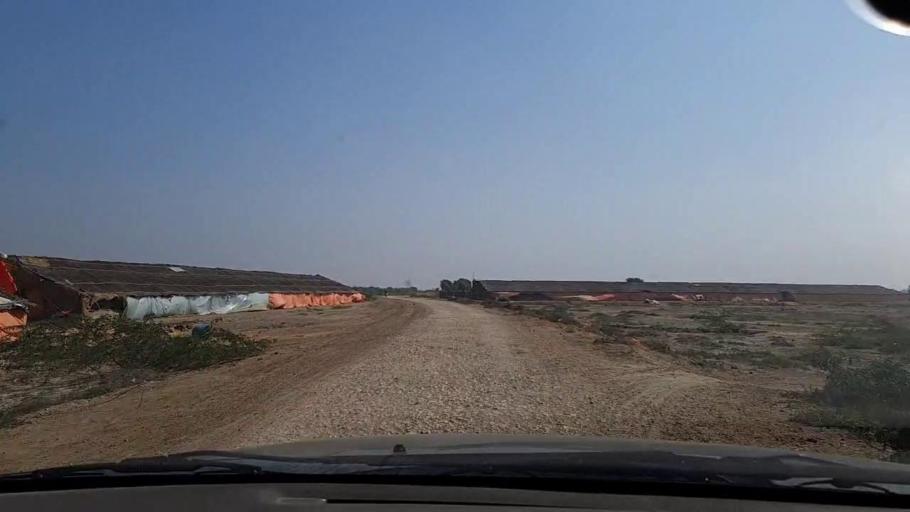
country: PK
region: Sindh
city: Chuhar Jamali
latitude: 24.4195
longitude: 67.8262
